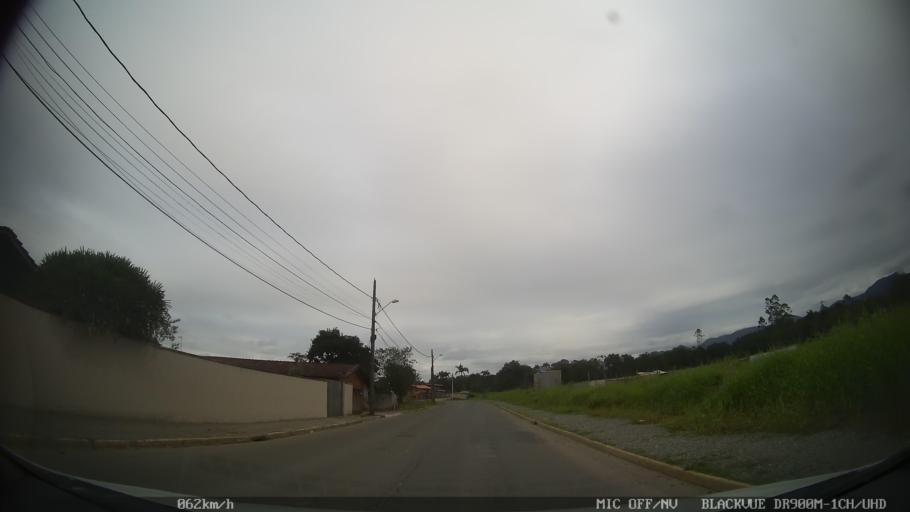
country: BR
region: Santa Catarina
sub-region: Joinville
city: Joinville
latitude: -26.3350
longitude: -48.9095
